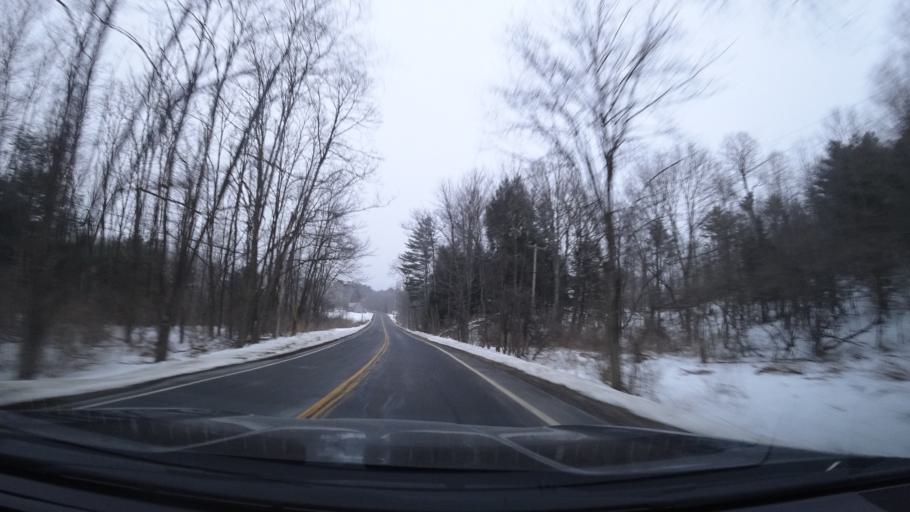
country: US
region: New York
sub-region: Washington County
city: Greenwich
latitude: 43.1544
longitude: -73.4182
